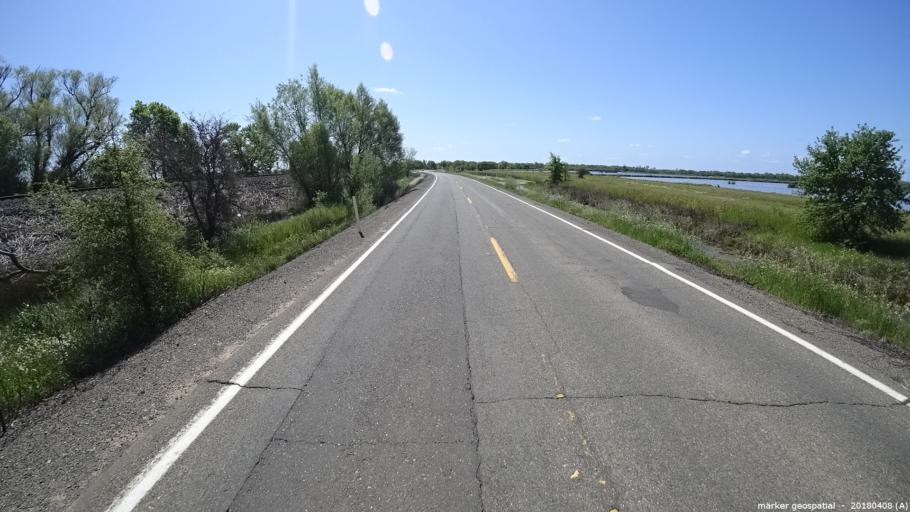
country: US
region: California
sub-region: San Joaquin County
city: Thornton
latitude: 38.2749
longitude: -121.4392
